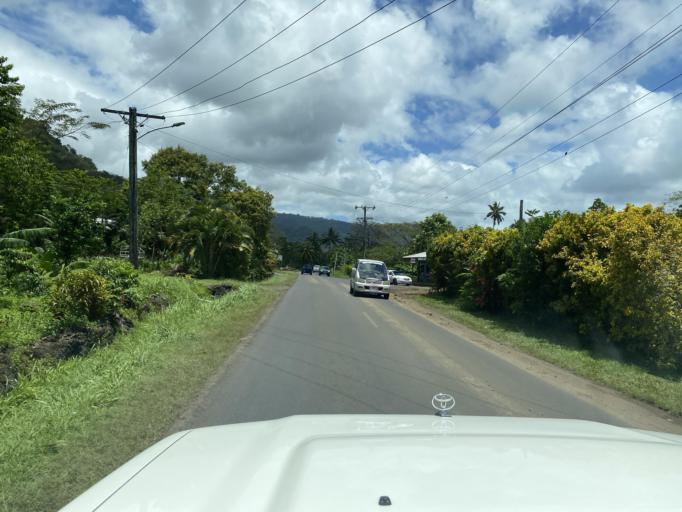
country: WS
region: Tuamasaga
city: Apia
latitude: -13.8486
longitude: -171.7787
